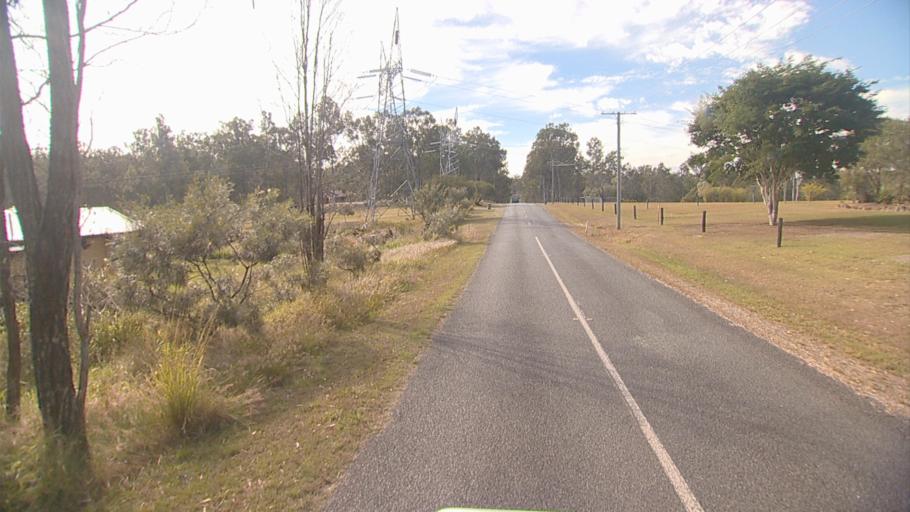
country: AU
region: Queensland
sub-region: Logan
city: North Maclean
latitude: -27.7418
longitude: 152.9743
